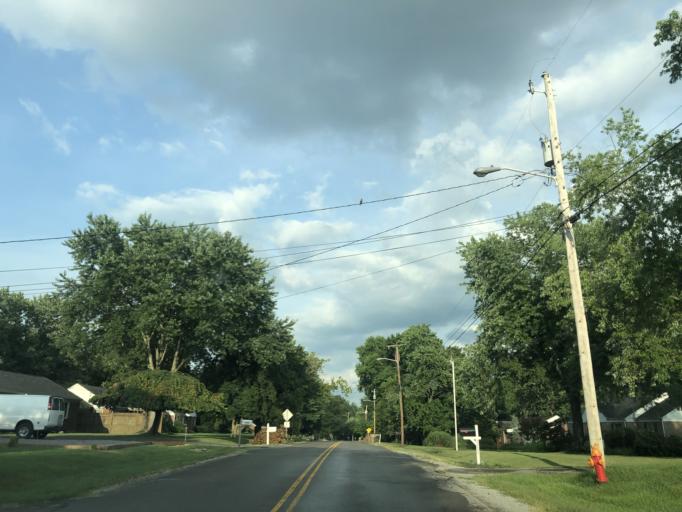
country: US
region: Tennessee
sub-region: Davidson County
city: Lakewood
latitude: 36.1569
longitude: -86.6728
